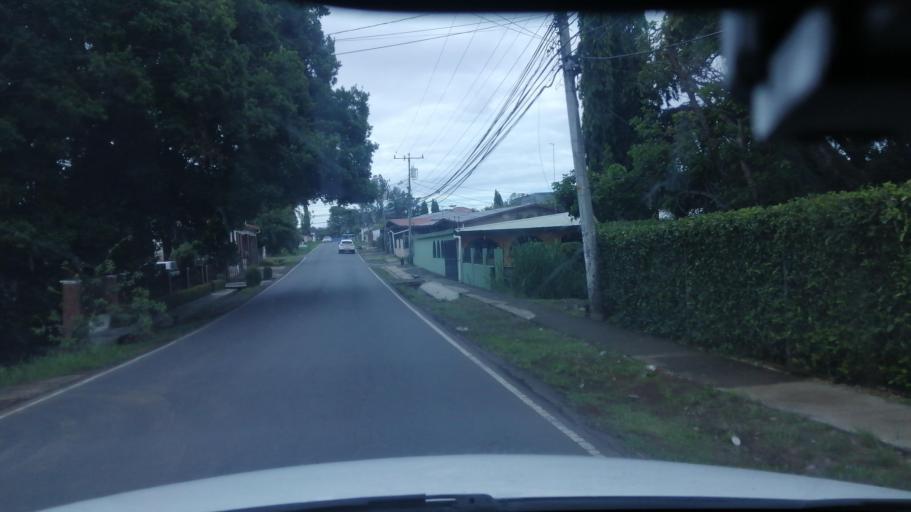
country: PA
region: Chiriqui
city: David
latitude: 8.4174
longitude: -82.4375
